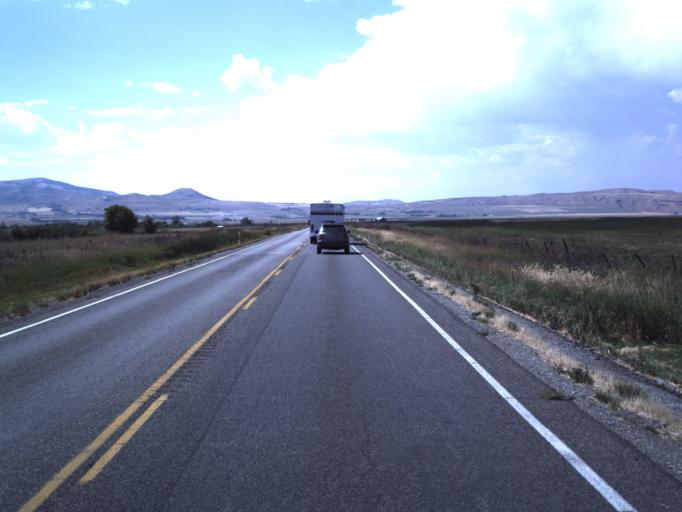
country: US
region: Utah
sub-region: Cache County
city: Benson
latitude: 41.7429
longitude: -111.9169
